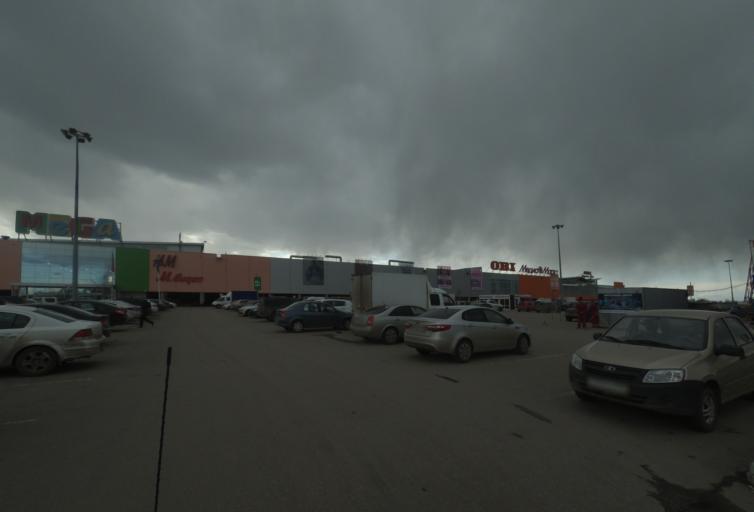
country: RU
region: Nizjnij Novgorod
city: Afonino
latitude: 56.2265
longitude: 44.0740
